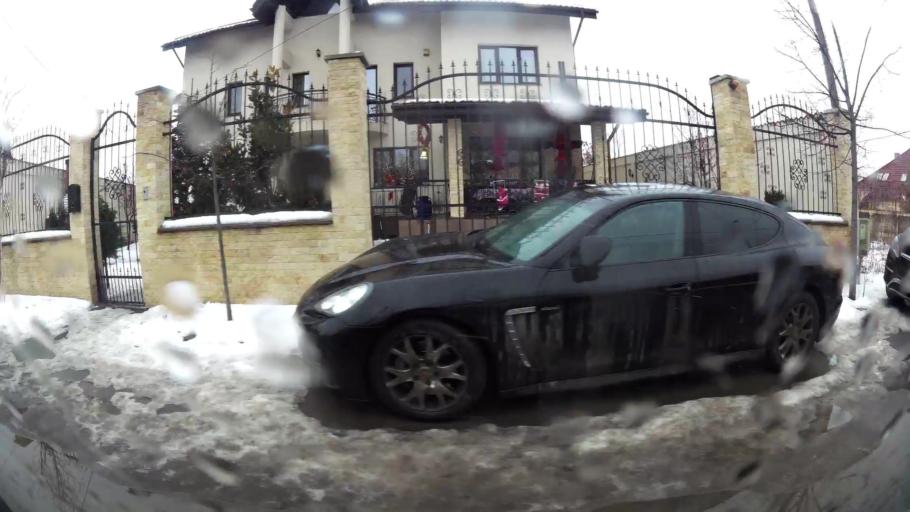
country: RO
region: Ilfov
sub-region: Comuna Chiajna
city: Rosu
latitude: 44.4074
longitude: 26.0113
